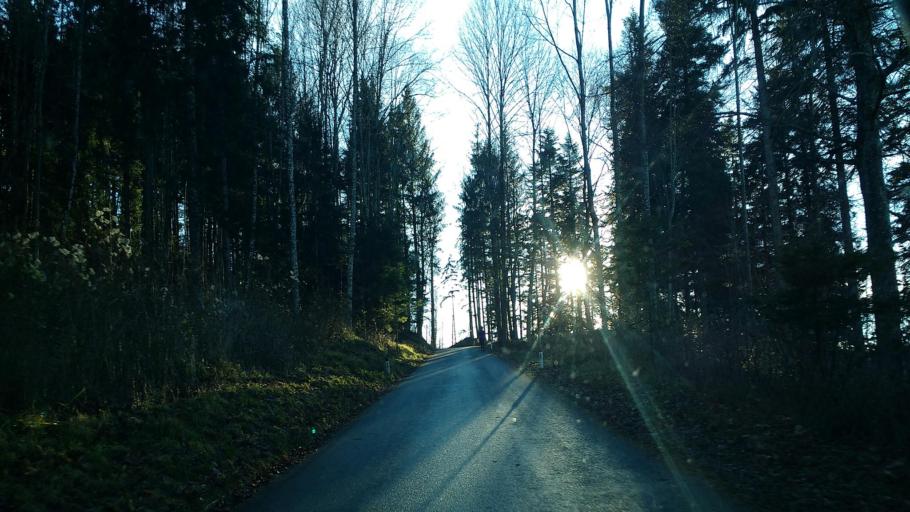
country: AT
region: Upper Austria
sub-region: Politischer Bezirk Kirchdorf an der Krems
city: Micheldorf in Oberoesterreich
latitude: 47.9109
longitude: 14.1476
